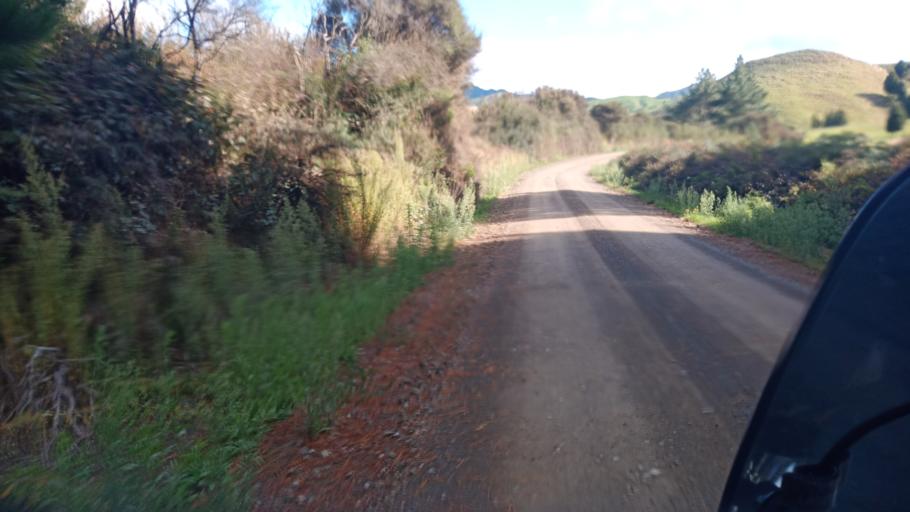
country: NZ
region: Bay of Plenty
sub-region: Opotiki District
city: Opotiki
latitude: -38.4600
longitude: 177.4186
